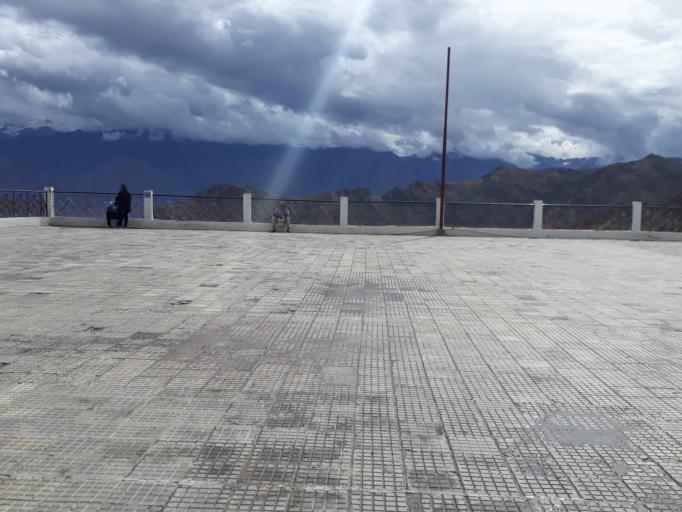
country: IN
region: Kashmir
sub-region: Ladakh
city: Leh
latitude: 34.1737
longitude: 77.5752
